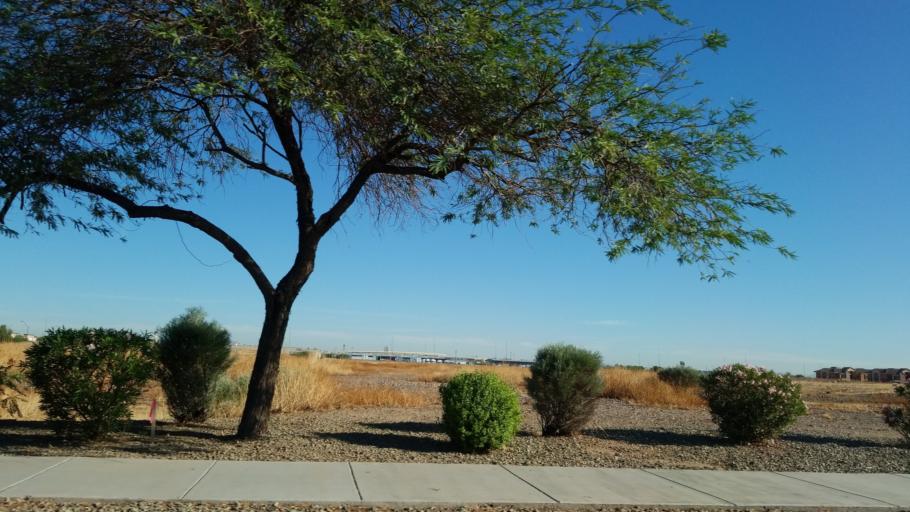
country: US
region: Arizona
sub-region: Maricopa County
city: Tolleson
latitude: 33.4503
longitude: -112.2709
